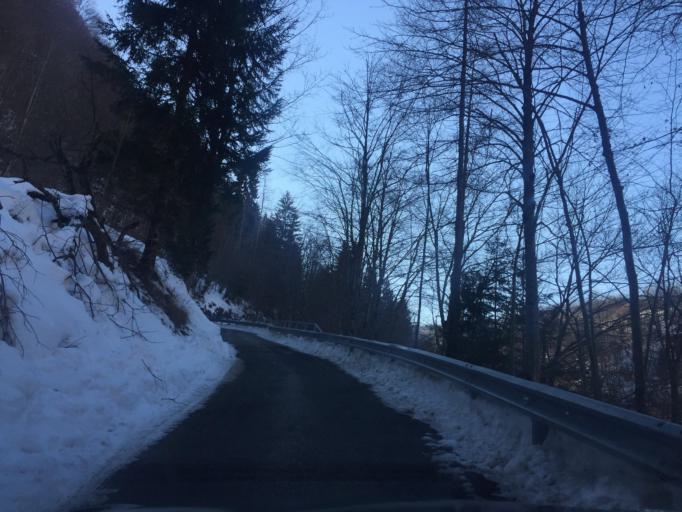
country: IT
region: Friuli Venezia Giulia
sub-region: Provincia di Udine
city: Lauco
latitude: 46.4396
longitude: 12.9735
